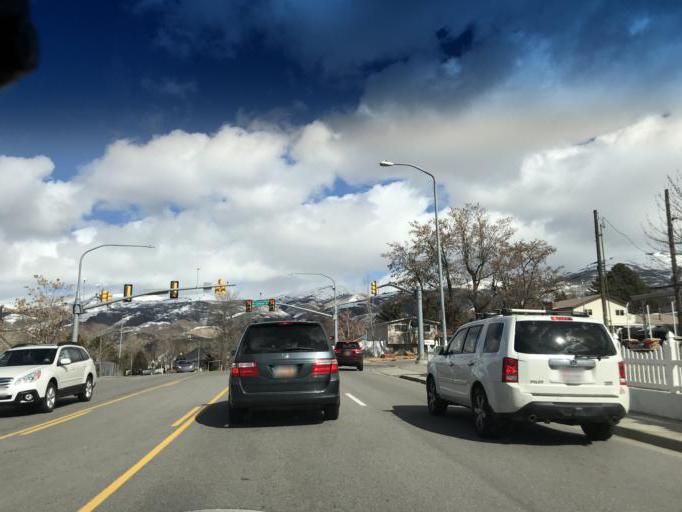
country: US
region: Utah
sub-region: Davis County
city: Woods Cross
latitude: 40.8627
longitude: -111.8816
